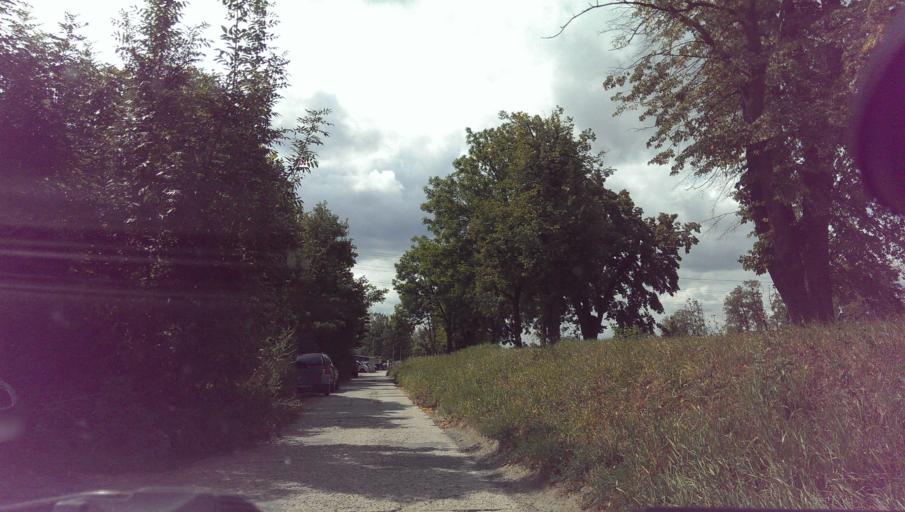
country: CZ
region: Zlin
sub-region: Okres Uherske Hradiste
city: Uherske Hradiste
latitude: 49.0758
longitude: 17.4753
